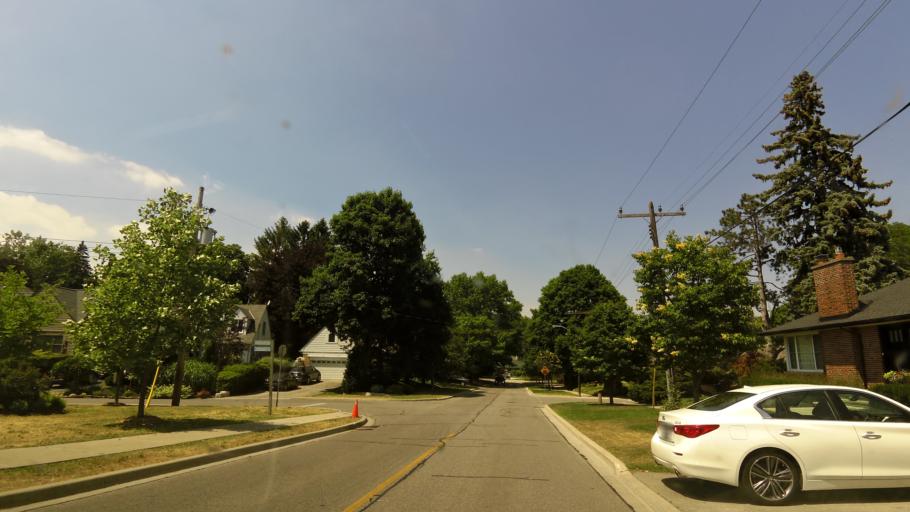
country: CA
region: Ontario
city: Etobicoke
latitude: 43.6405
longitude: -79.4953
